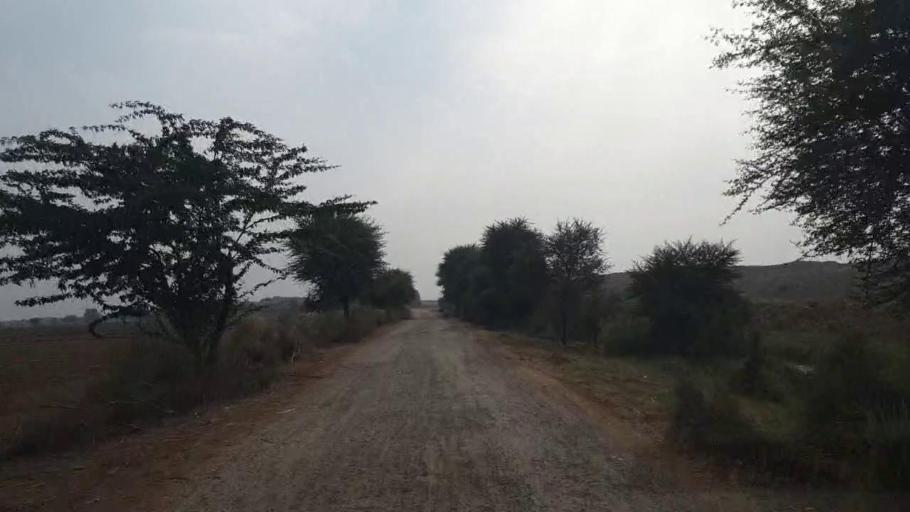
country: PK
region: Sindh
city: Sann
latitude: 26.0180
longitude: 68.1442
